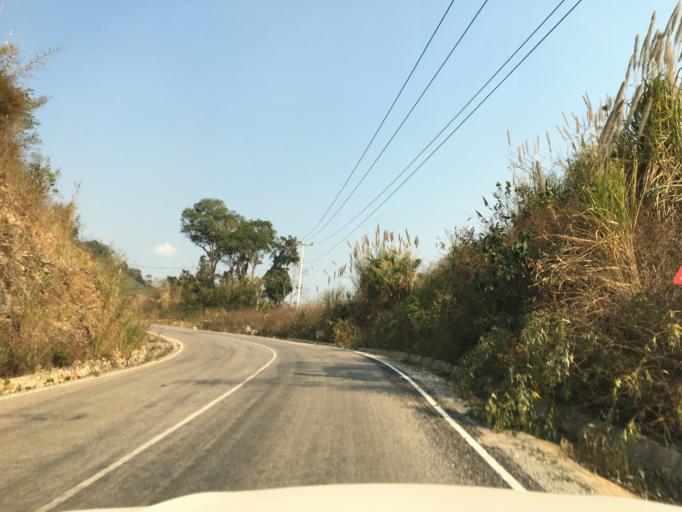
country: LA
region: Houaphan
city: Xam Nua
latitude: 20.5685
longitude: 104.0524
